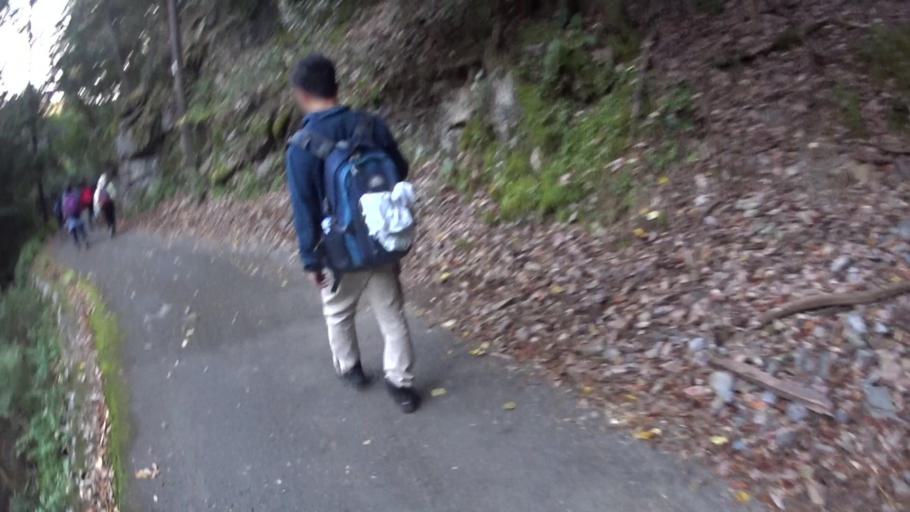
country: JP
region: Kyoto
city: Kameoka
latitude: 35.0468
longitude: 135.6540
